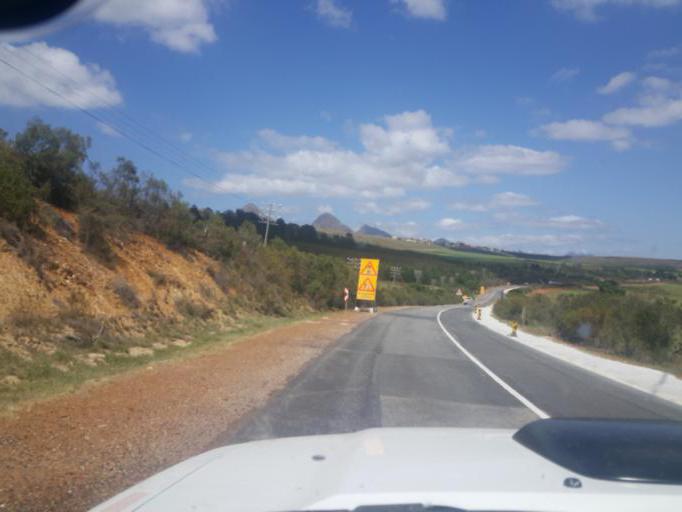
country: ZA
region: Eastern Cape
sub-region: Cacadu District Municipality
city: Kareedouw
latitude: -33.9497
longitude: 24.3291
